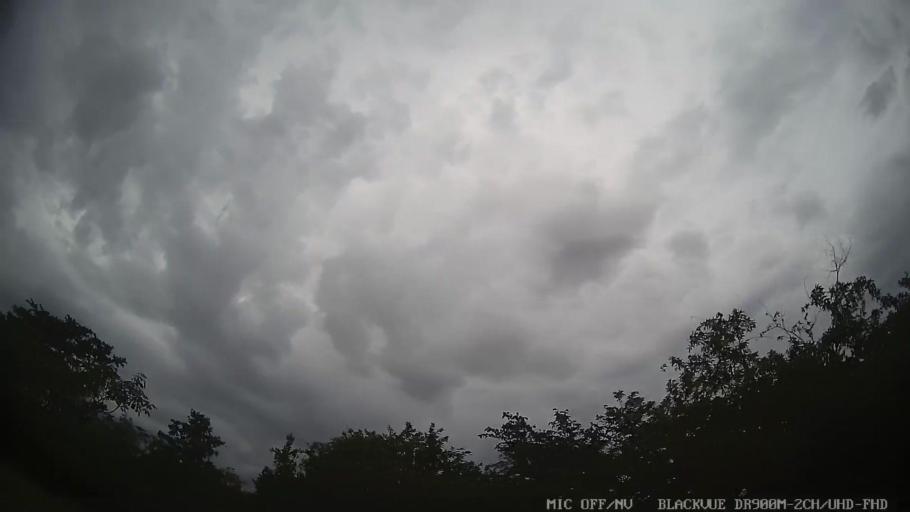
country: BR
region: Sao Paulo
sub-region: Amparo
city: Amparo
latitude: -22.6984
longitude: -46.7582
